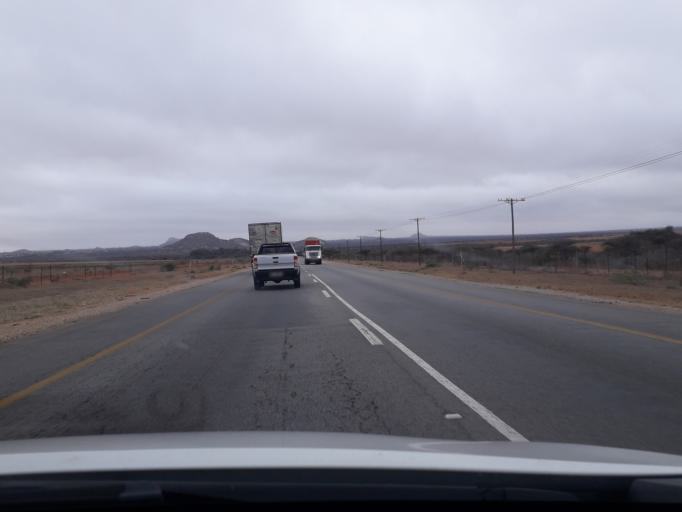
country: ZA
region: Limpopo
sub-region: Capricorn District Municipality
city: Mankoeng
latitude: -23.5574
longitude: 29.6856
